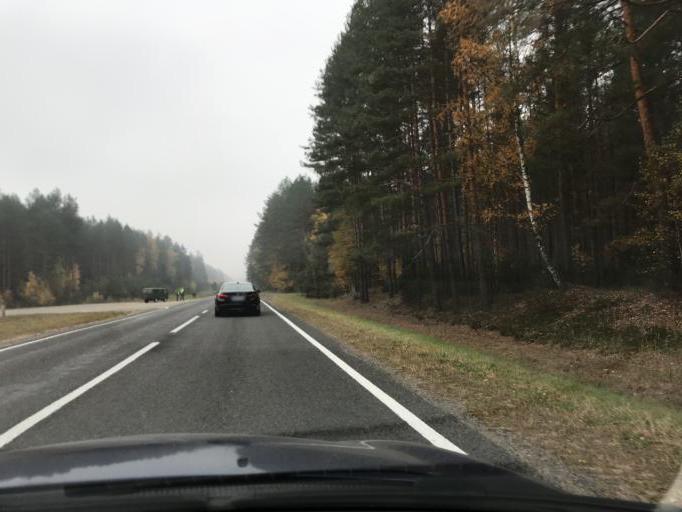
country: LT
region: Alytaus apskritis
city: Druskininkai
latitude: 53.8864
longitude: 23.9080
